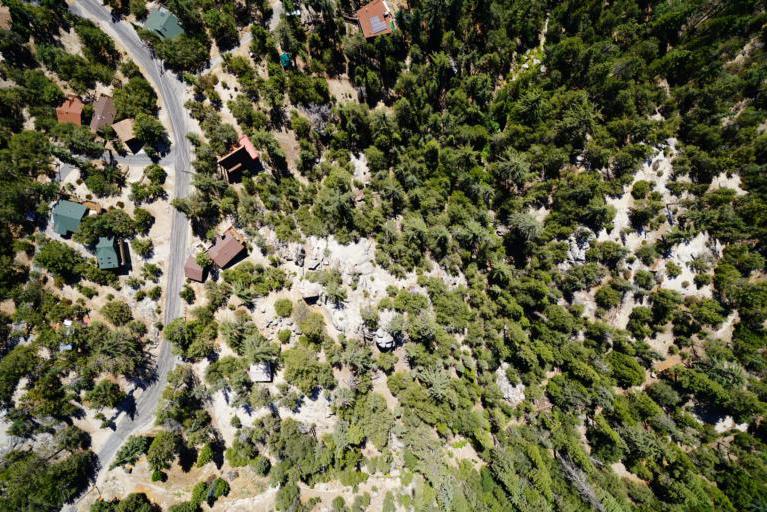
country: US
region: California
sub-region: Riverside County
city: Idyllwild-Pine Cove
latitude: 33.7662
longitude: -116.7355
